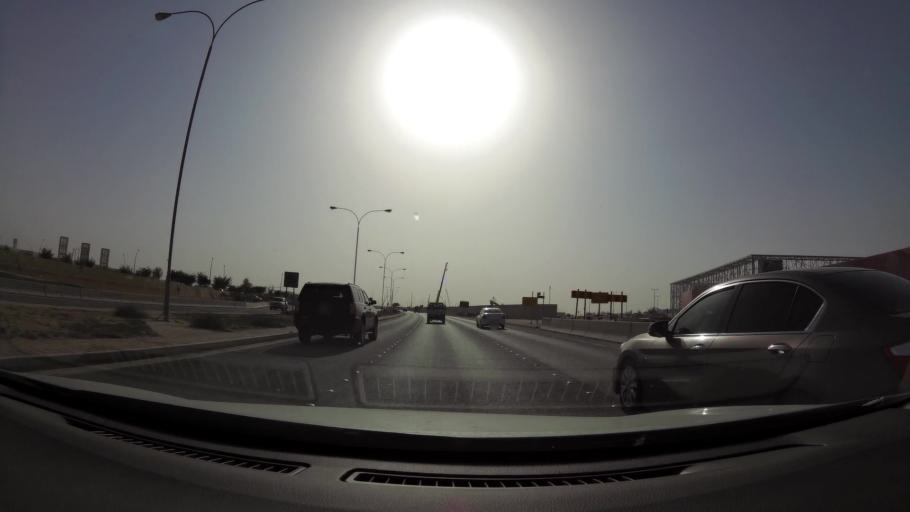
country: QA
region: Baladiyat ar Rayyan
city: Ar Rayyan
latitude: 25.3192
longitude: 51.4350
